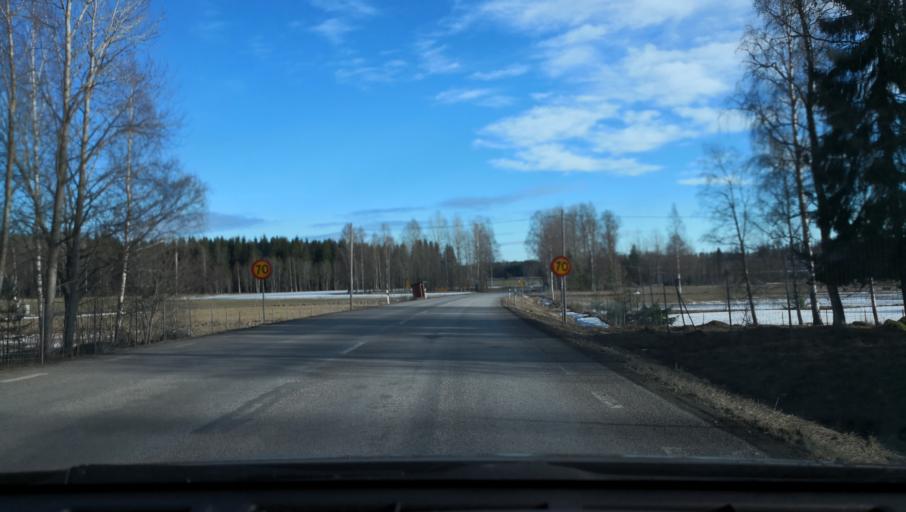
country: SE
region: Uppsala
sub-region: Osthammars Kommun
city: Osterbybruk
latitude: 60.1669
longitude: 17.9720
